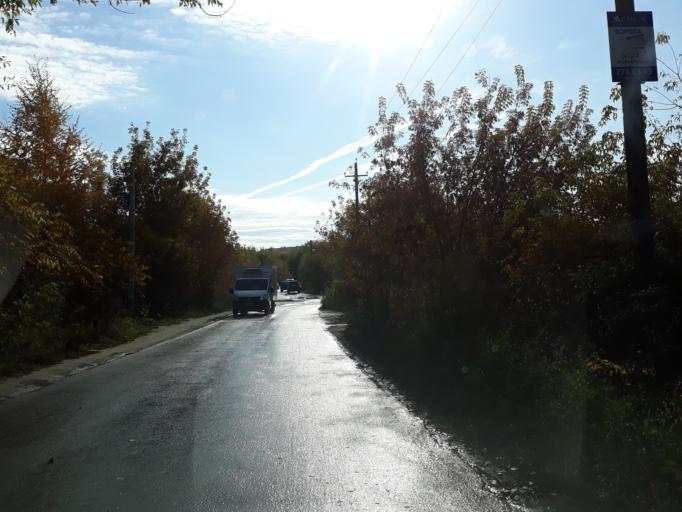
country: RU
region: Nizjnij Novgorod
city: Nizhniy Novgorod
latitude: 56.2509
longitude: 43.9908
